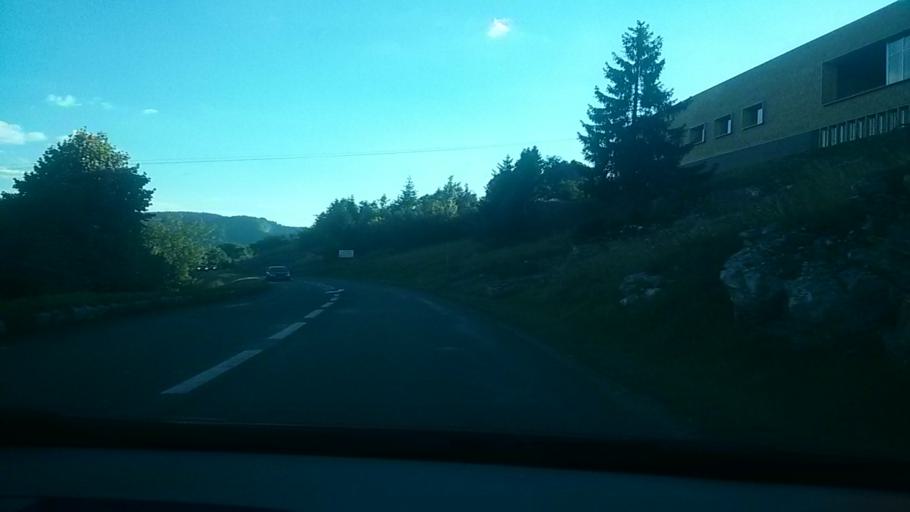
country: FR
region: Franche-Comte
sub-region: Departement du Jura
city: Saint-Claude
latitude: 46.3782
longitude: 5.9228
